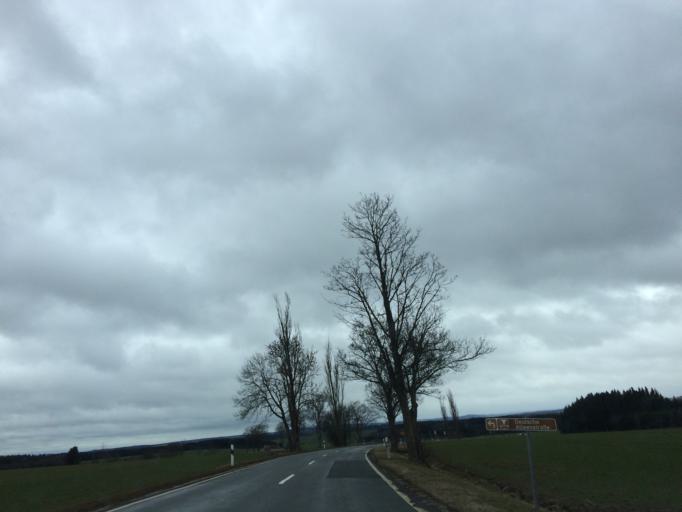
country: DE
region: Thuringia
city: Moxa
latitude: 50.6575
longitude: 11.6320
